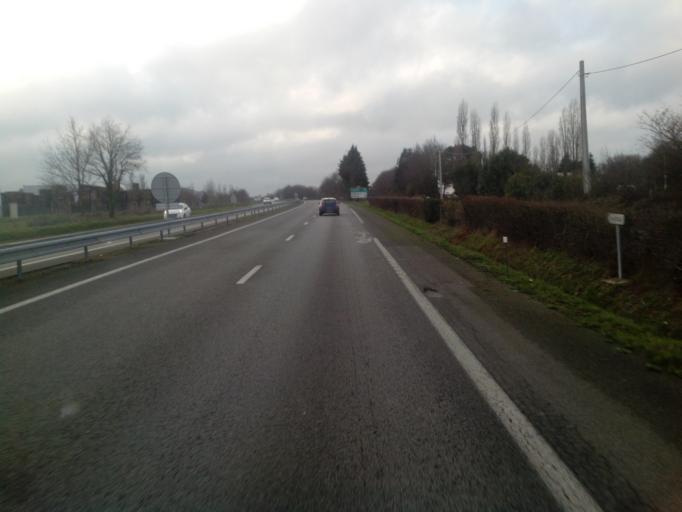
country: FR
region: Brittany
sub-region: Departement du Morbihan
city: Guegon
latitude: 47.9465
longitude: -2.5864
